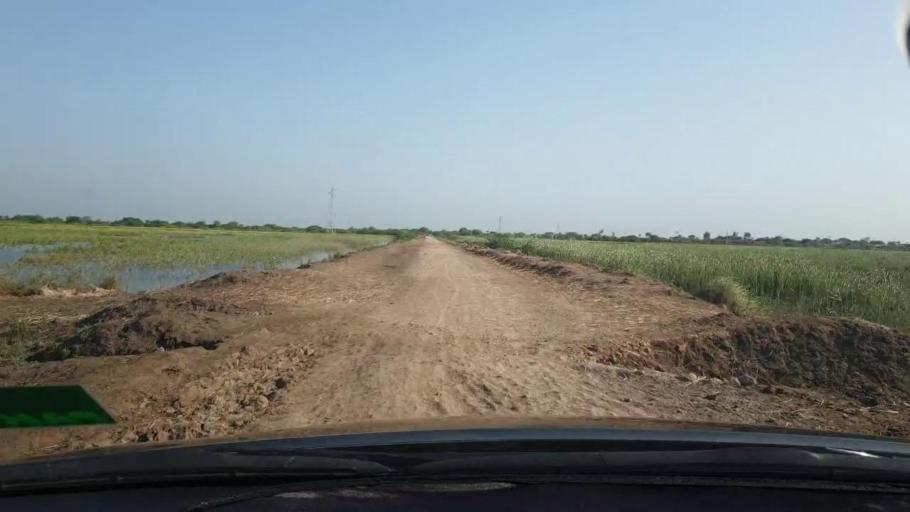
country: PK
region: Sindh
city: Tando Bago
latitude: 24.7155
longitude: 68.9522
